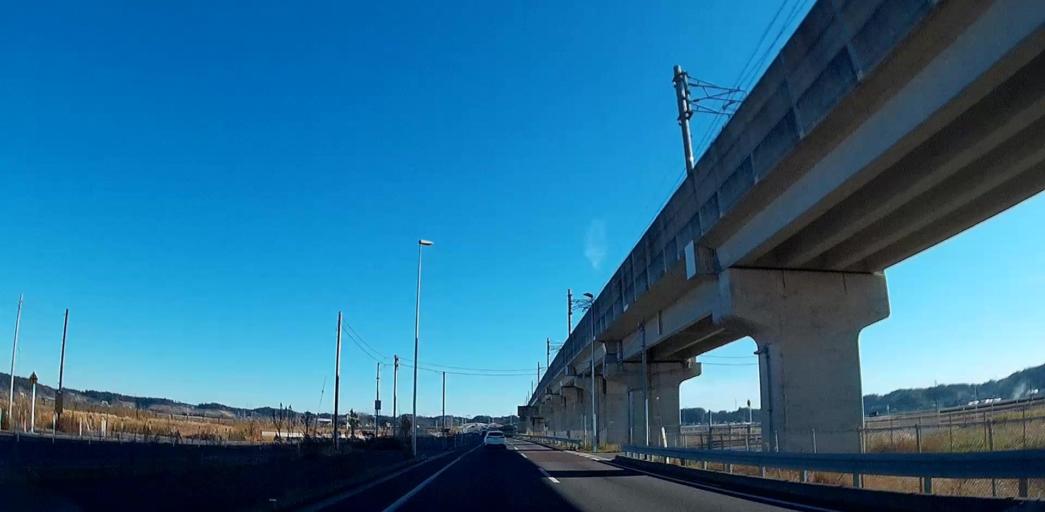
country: JP
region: Chiba
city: Narita
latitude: 35.7962
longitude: 140.2686
